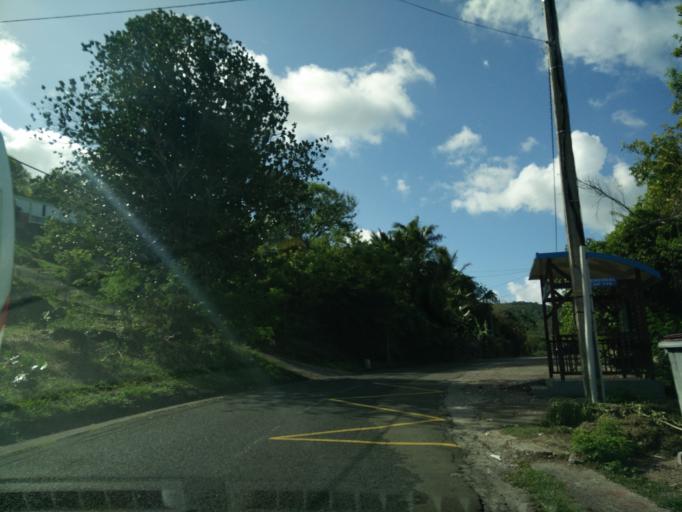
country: MQ
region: Martinique
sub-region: Martinique
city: Les Trois-Ilets
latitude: 14.4649
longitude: -61.0469
